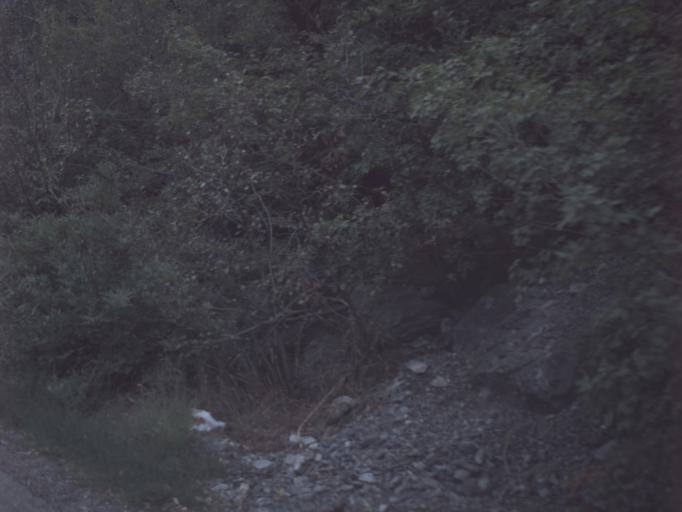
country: US
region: Utah
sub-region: Utah County
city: Cedar Hills
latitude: 40.4511
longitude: -111.6676
